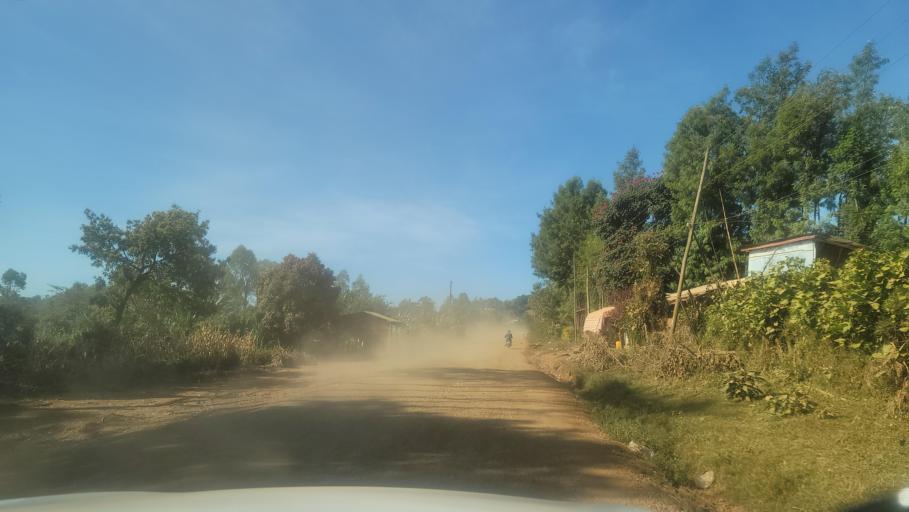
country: ET
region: Oromiya
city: Agaro
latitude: 7.8238
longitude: 36.5314
